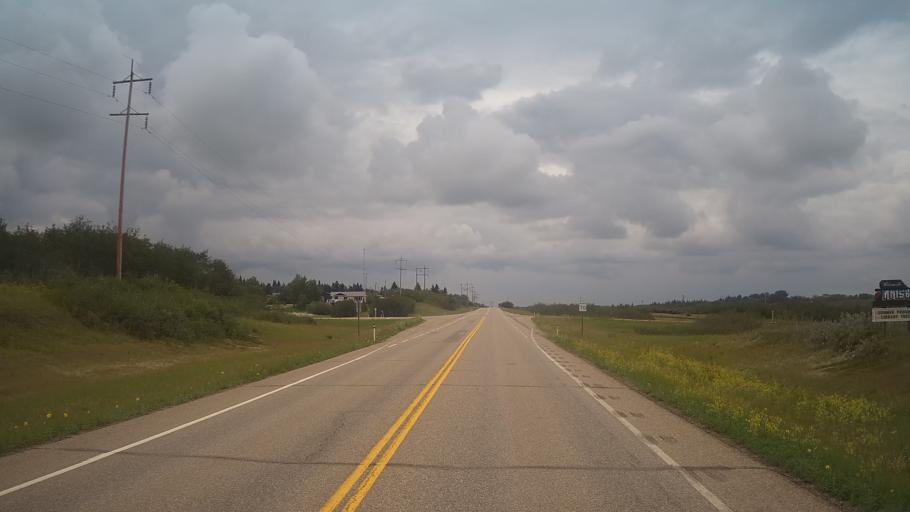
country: CA
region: Alberta
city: Wainwright
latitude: 52.5620
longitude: -111.0466
